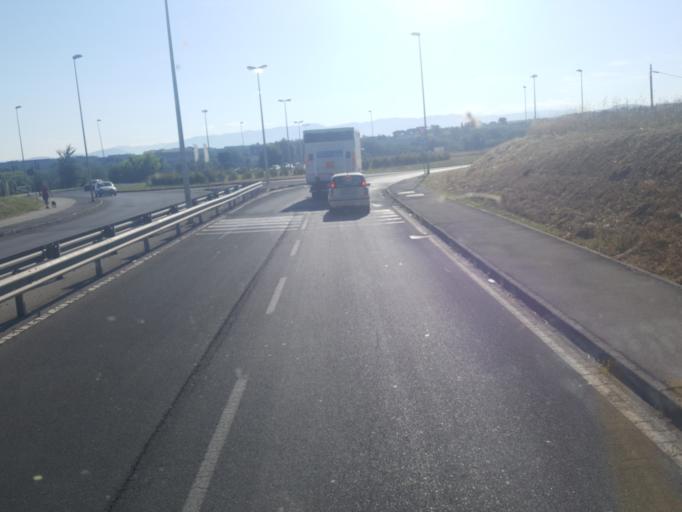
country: IT
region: Latium
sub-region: Citta metropolitana di Roma Capitale
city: Frascati
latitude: 41.8430
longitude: 12.6464
